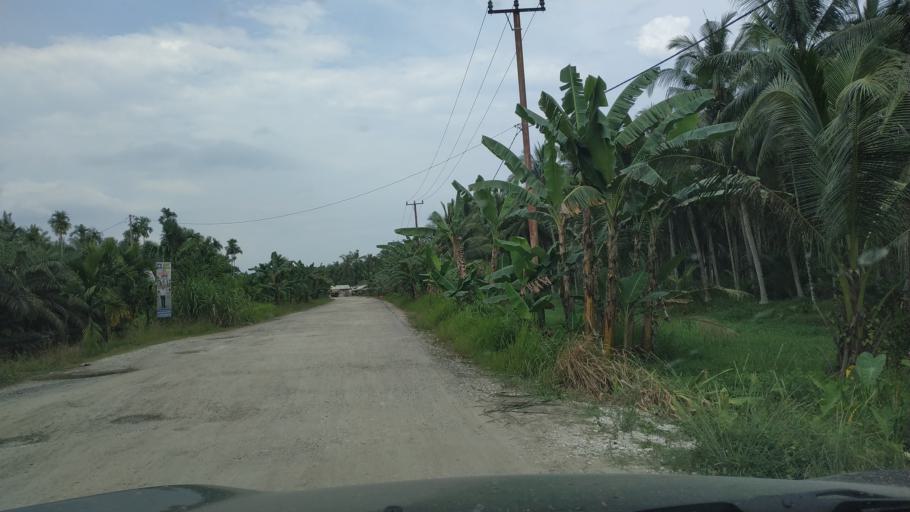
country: ID
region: Riau
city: Sungaisalak
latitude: -0.5190
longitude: 103.0029
